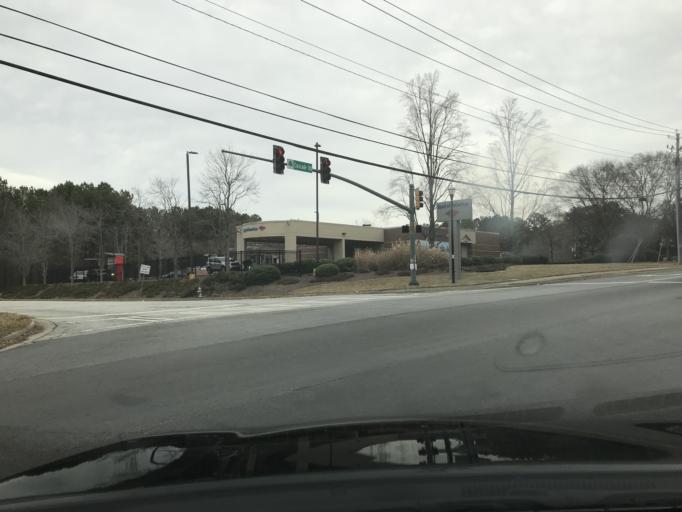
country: US
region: Georgia
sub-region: Fulton County
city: East Point
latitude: 33.7230
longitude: -84.5010
